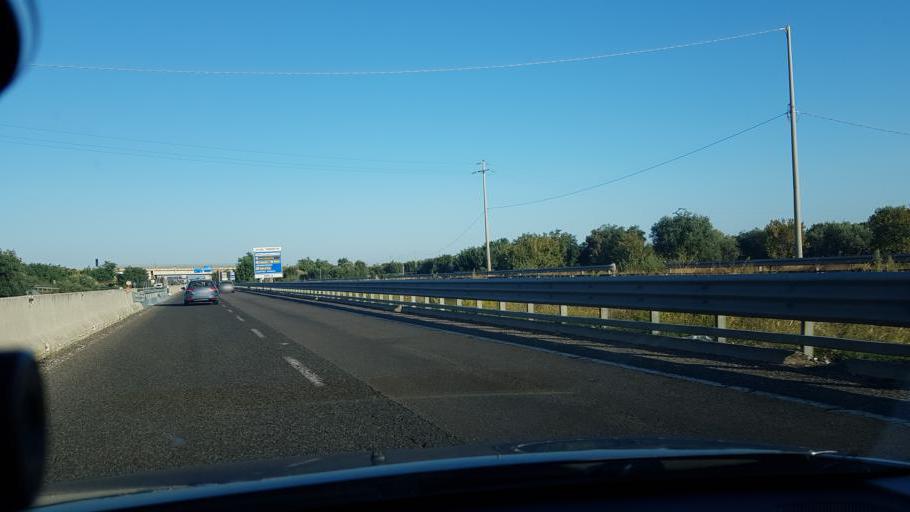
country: IT
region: Apulia
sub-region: Provincia di Brindisi
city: Fasano
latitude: 40.8483
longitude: 17.3602
